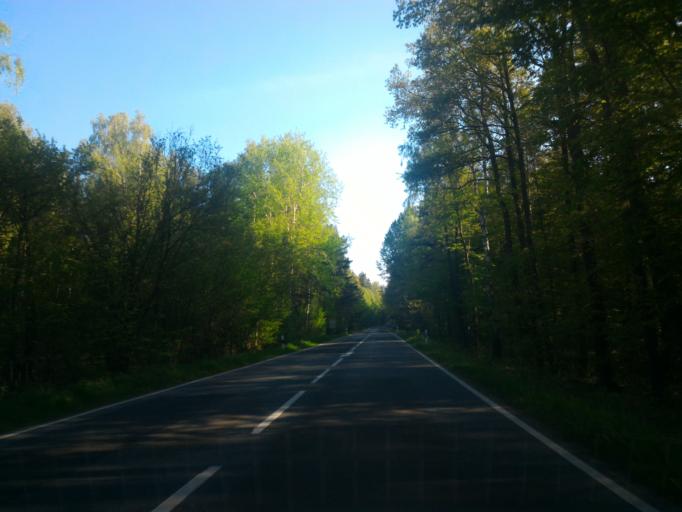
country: DE
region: Saxony
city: Grossschonau
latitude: 50.9193
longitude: 14.6608
